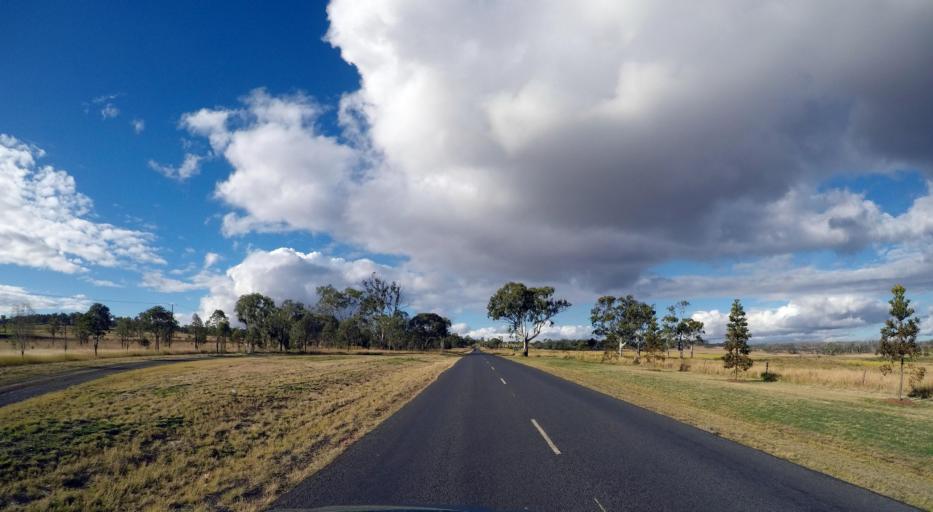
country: AU
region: Queensland
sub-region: Toowoomba
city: Westbrook
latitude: -27.7052
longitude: 151.6536
